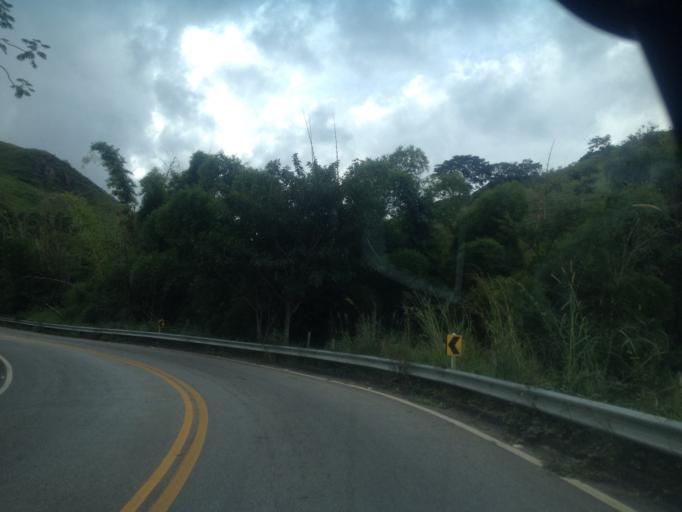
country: BR
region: Rio de Janeiro
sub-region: Quatis
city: Quatis
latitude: -22.3849
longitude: -44.2622
